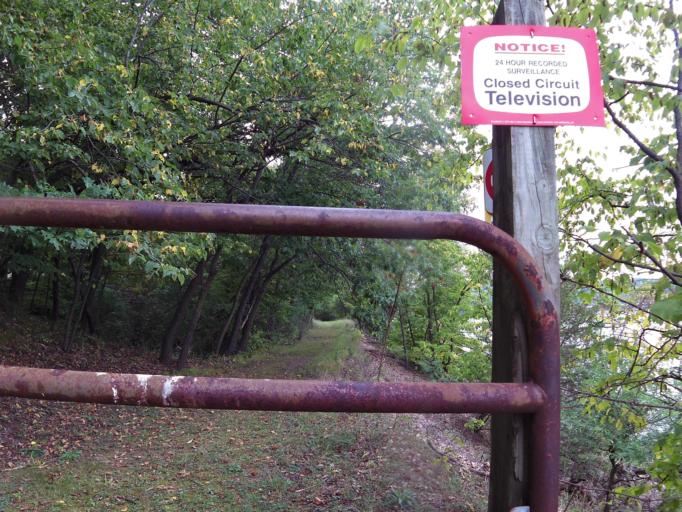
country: US
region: Minnesota
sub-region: Washington County
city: Afton
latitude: 44.8729
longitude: -92.7688
